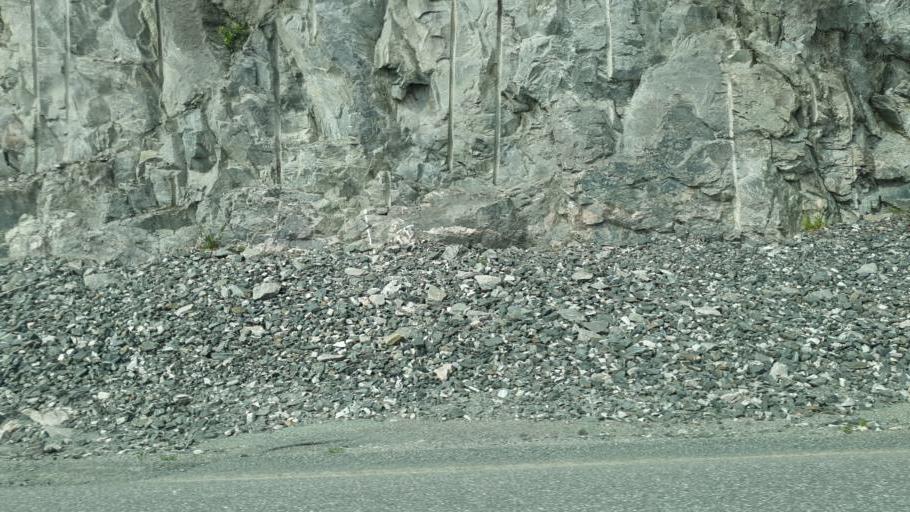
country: NO
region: Sor-Trondelag
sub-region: Trondheim
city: Trondheim
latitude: 63.5973
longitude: 10.4592
